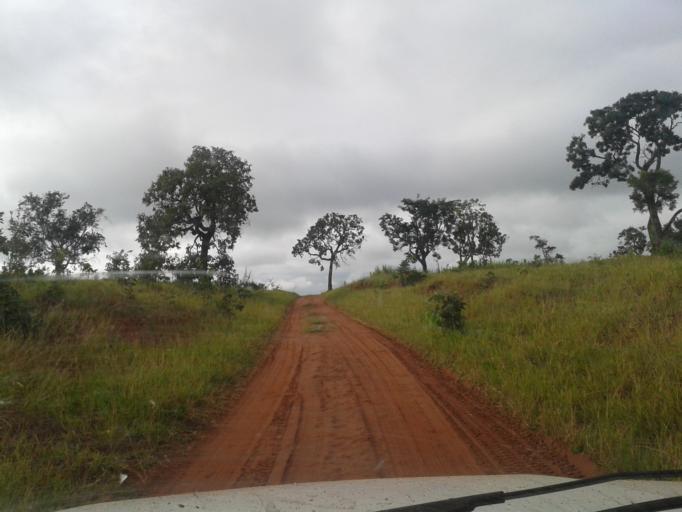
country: BR
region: Minas Gerais
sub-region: Campina Verde
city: Campina Verde
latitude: -19.4111
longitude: -49.6295
